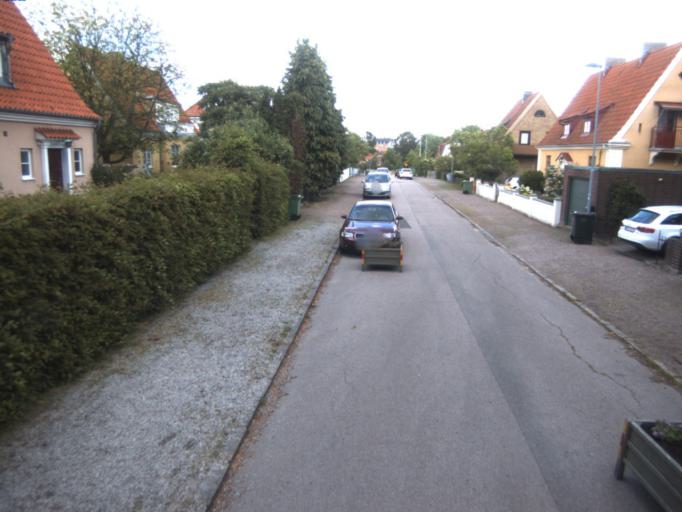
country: SE
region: Skane
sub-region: Helsingborg
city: Helsingborg
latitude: 56.0484
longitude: 12.7147
